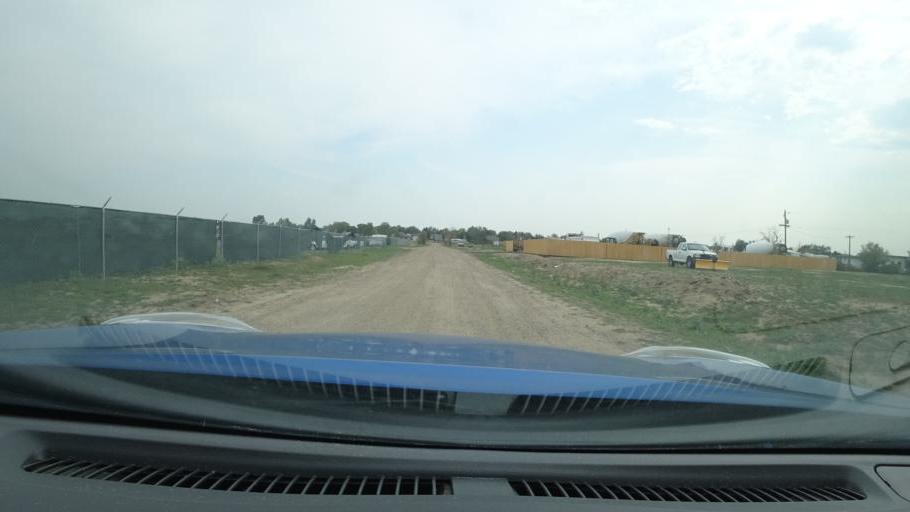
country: US
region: Colorado
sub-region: Adams County
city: Aurora
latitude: 39.7535
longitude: -104.7690
